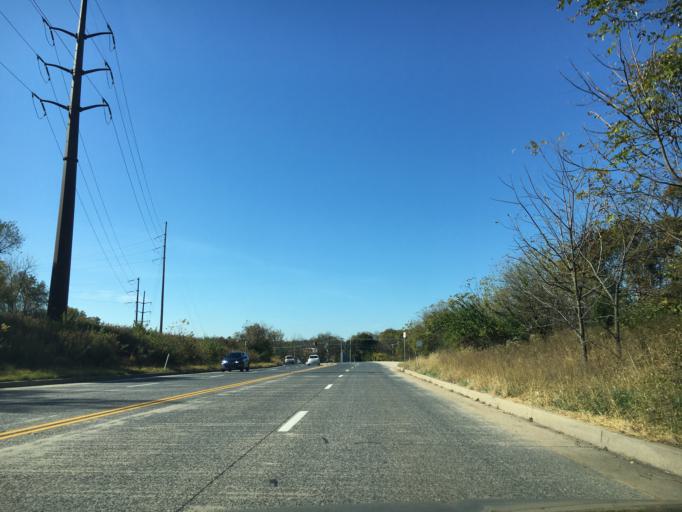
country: US
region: Pennsylvania
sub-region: Lehigh County
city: Fullerton
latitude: 40.6306
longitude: -75.4476
